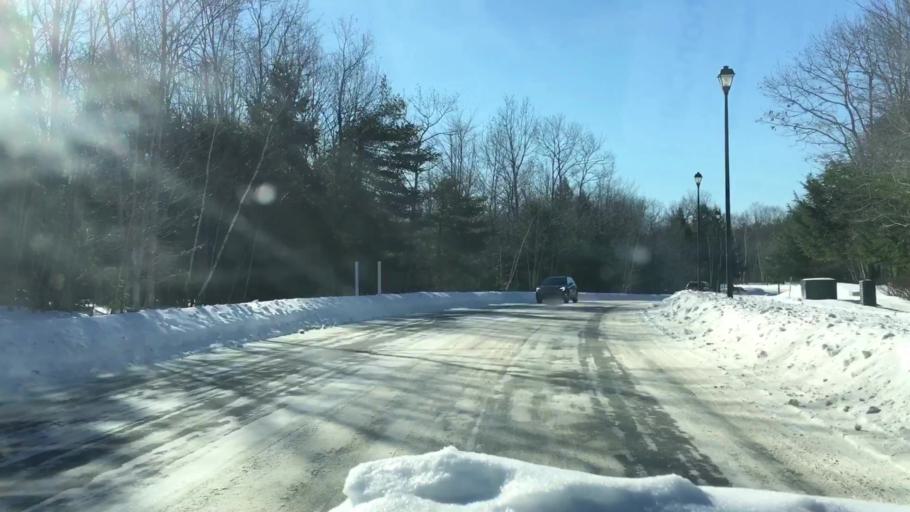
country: US
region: Maine
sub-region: Sagadahoc County
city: Topsham
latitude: 43.9424
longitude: -69.9536
